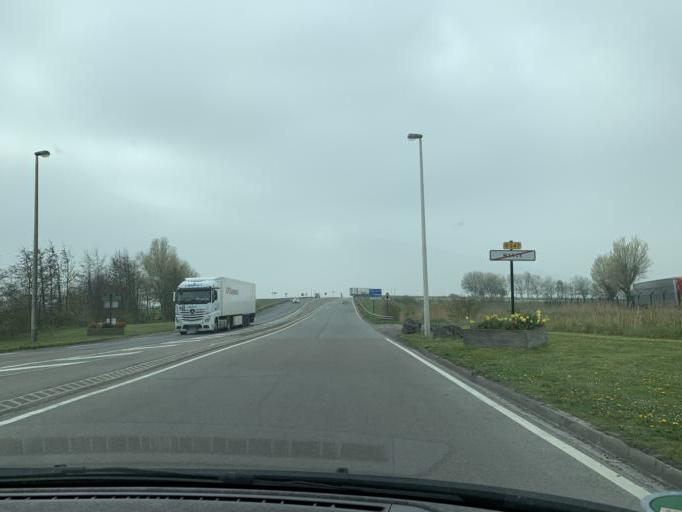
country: FR
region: Nord-Pas-de-Calais
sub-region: Departement du Pas-de-Calais
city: Marck
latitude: 50.9407
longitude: 1.9403
